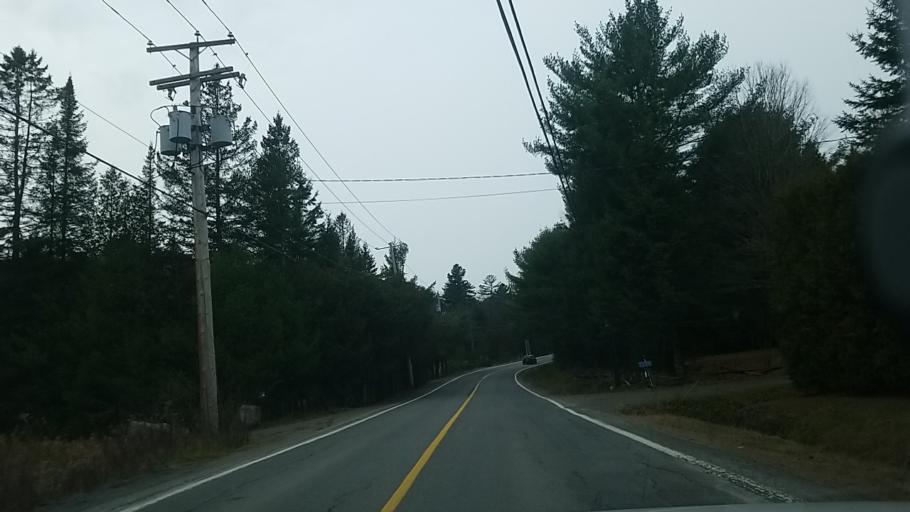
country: CA
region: Quebec
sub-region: Laurentides
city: Saint-Colomban
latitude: 45.7853
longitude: -74.1102
